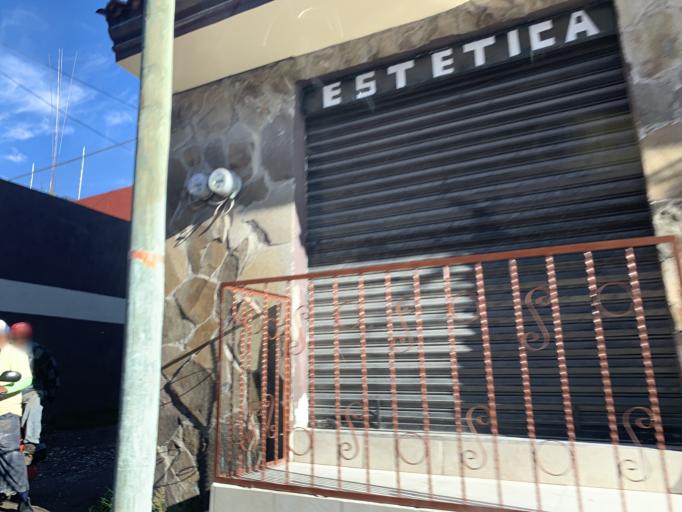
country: MX
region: Puebla
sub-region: Cuautlancingo
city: La Trinidad Chautenco
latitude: 19.0854
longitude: -98.2511
